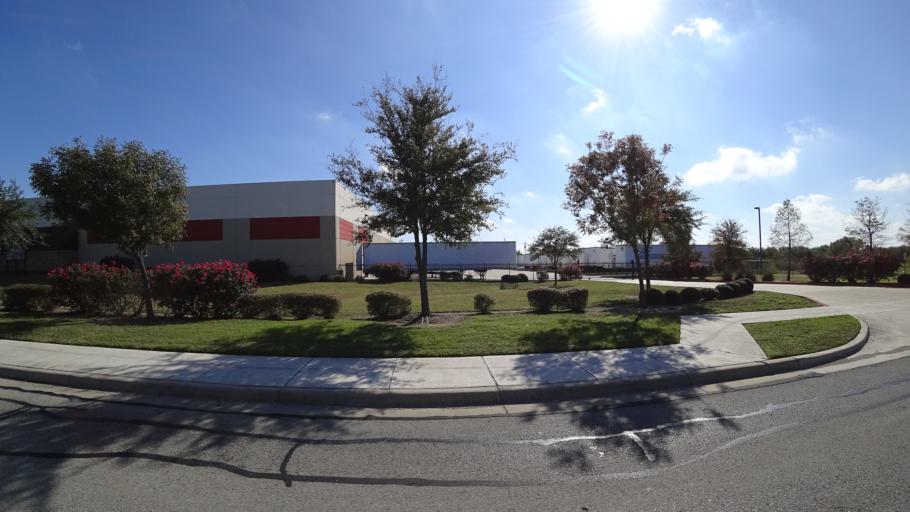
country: US
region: Texas
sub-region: Travis County
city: Windemere
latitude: 30.4348
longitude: -97.6484
